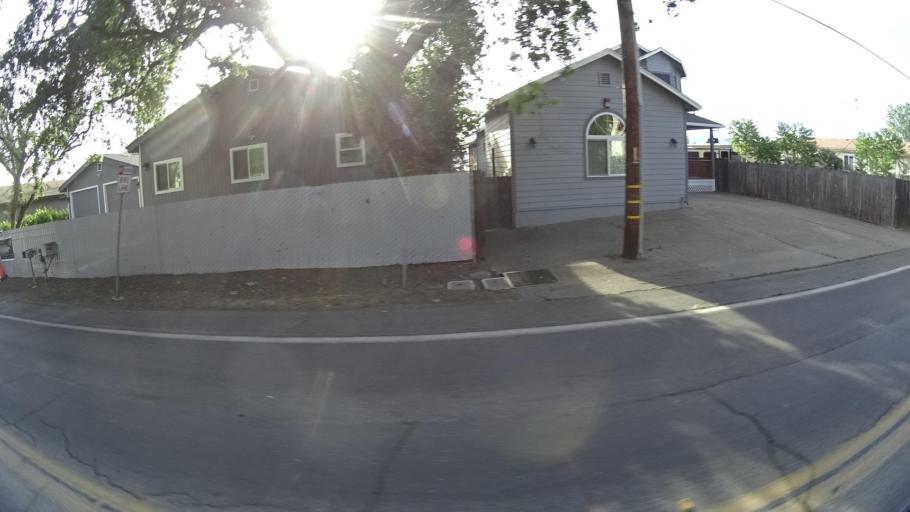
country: US
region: California
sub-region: Lake County
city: North Lakeport
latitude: 39.0665
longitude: -122.9133
